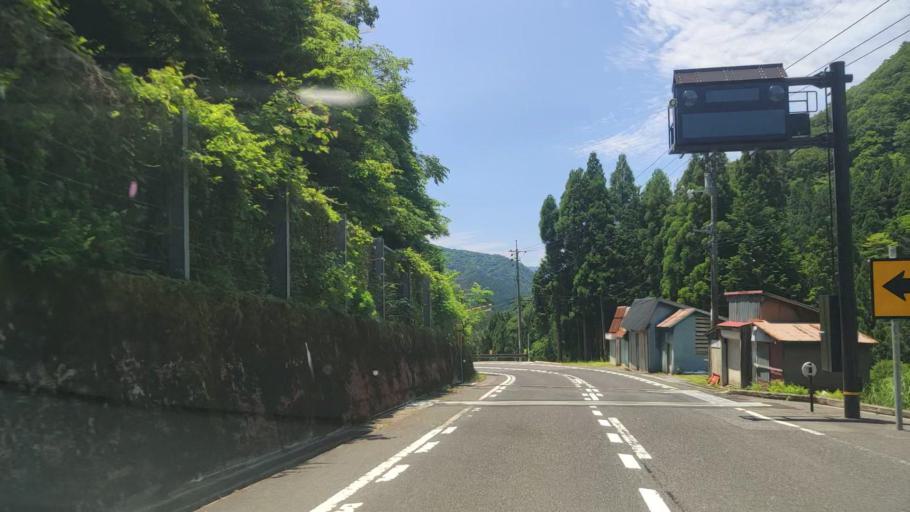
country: JP
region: Tottori
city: Tottori
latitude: 35.3557
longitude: 134.4737
